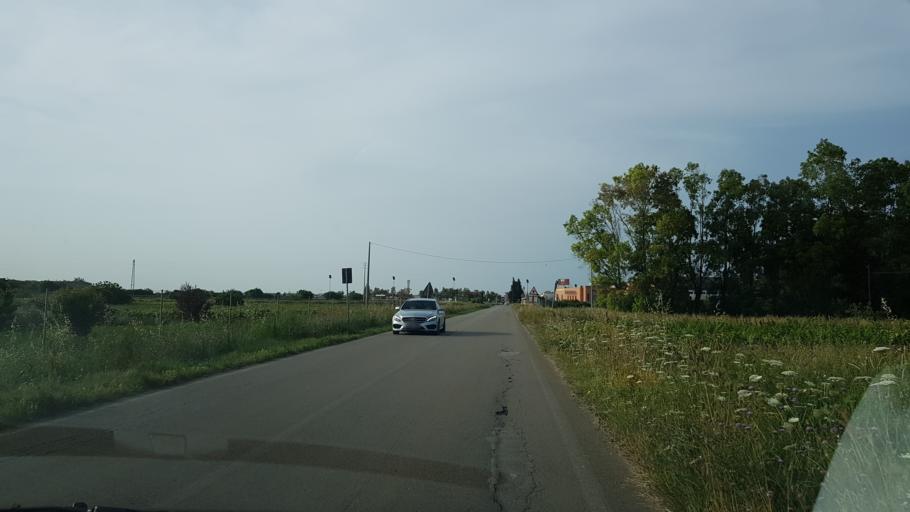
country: IT
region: Apulia
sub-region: Provincia di Brindisi
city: San Pancrazio Salentino
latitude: 40.4046
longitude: 17.8359
